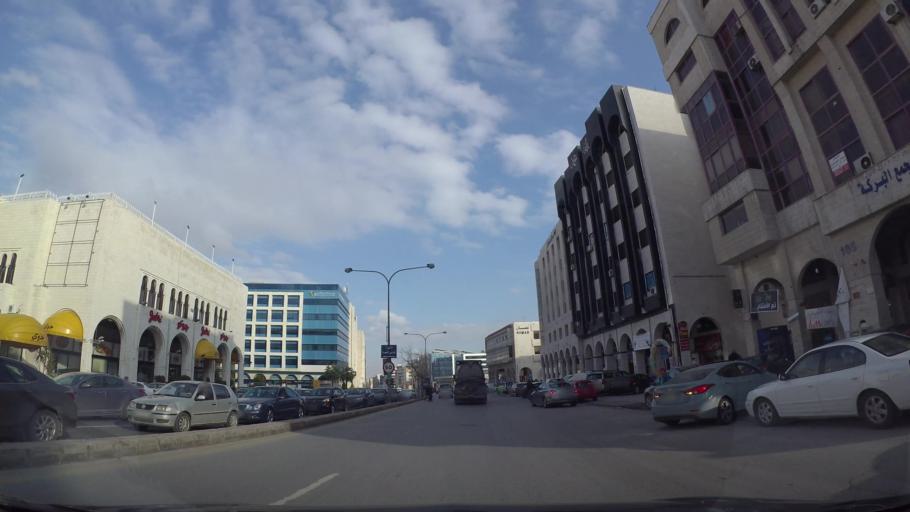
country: JO
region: Amman
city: Al Jubayhah
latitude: 31.9873
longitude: 35.8767
